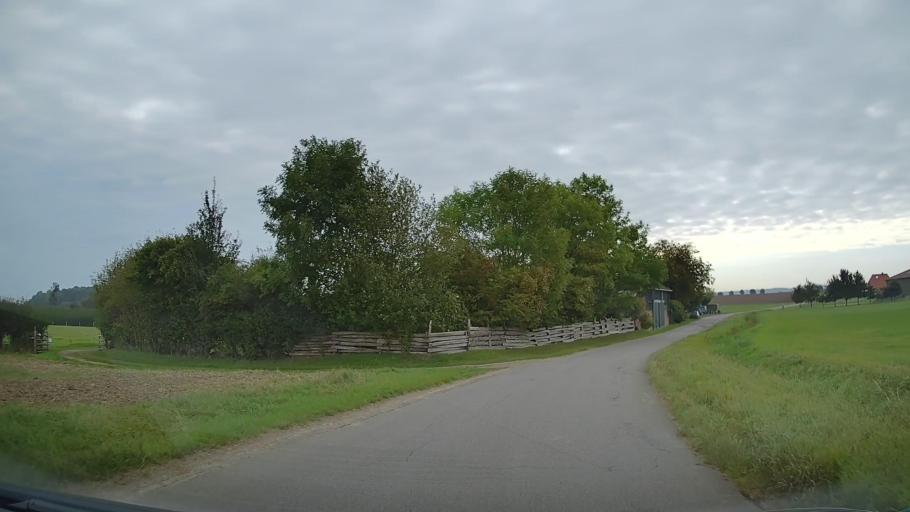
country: DE
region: Schleswig-Holstein
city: Hohenfelde
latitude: 54.3747
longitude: 10.5433
